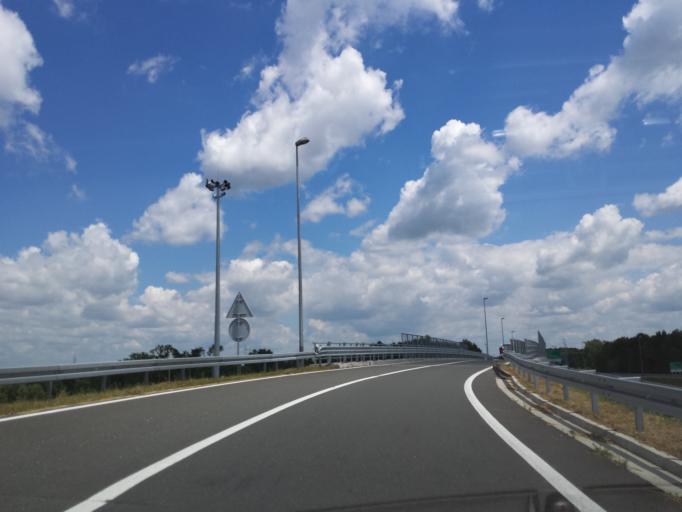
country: HR
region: Sisacko-Moslavacka
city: Lekenik
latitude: 45.5633
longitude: 16.2170
